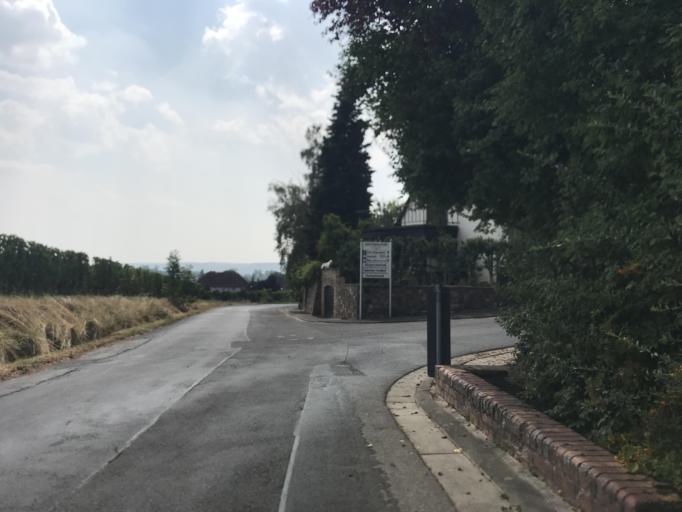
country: DE
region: Rheinland-Pfalz
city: Oestrich-Winkel
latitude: 50.0119
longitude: 8.0337
